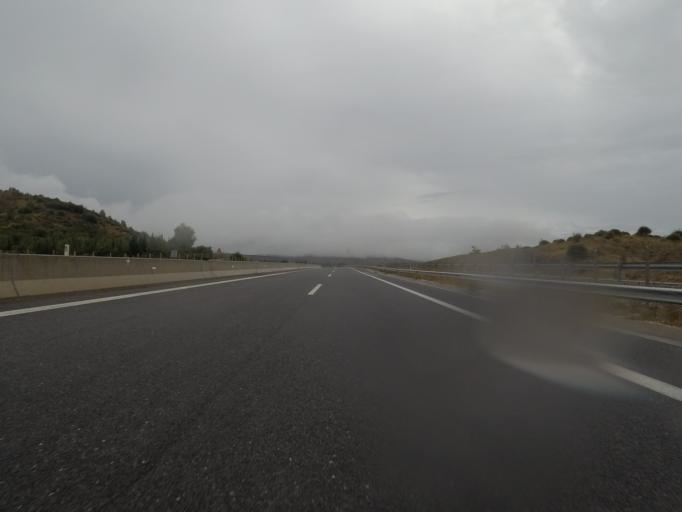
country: GR
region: Peloponnese
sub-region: Nomos Arkadias
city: Megalopoli
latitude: 37.3878
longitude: 22.2801
